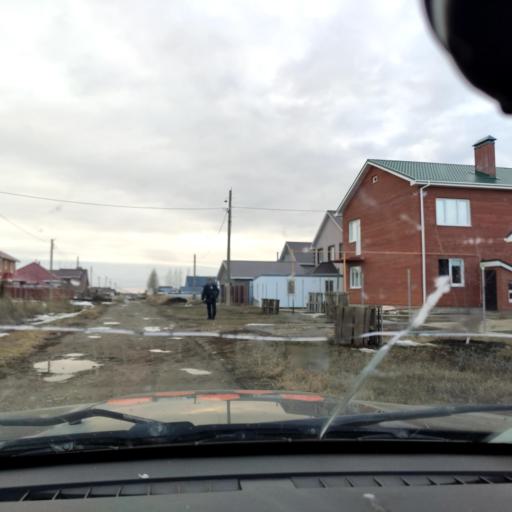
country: RU
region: Samara
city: Podstepki
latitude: 53.5262
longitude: 49.1686
